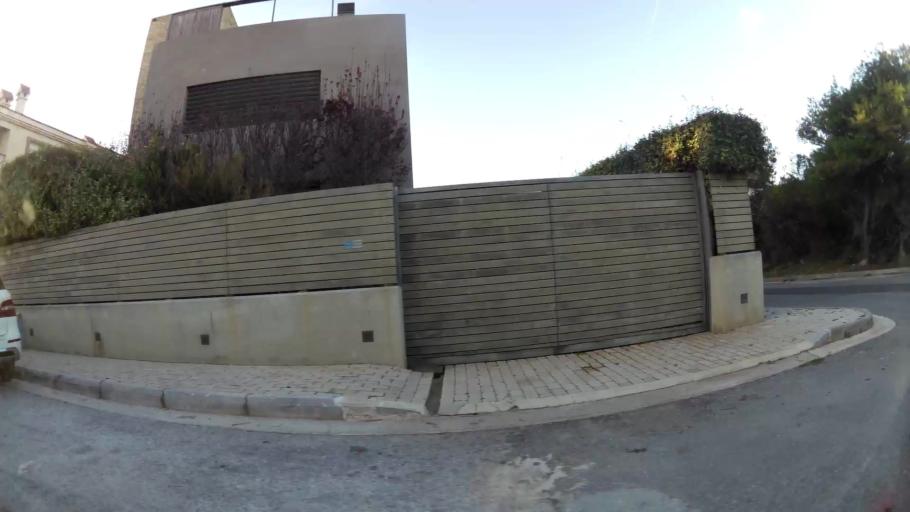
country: GR
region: Attica
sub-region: Nomarchia Anatolikis Attikis
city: Rafina
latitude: 38.0079
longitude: 24.0216
